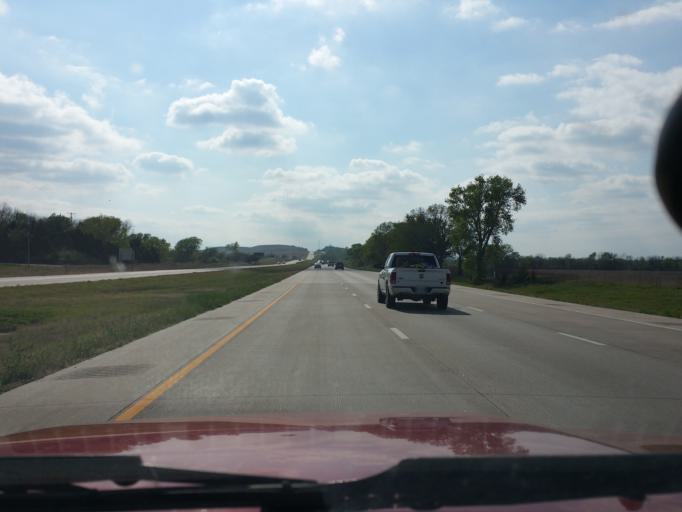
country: US
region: Kansas
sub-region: Pottawatomie County
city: Saint Marys
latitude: 39.0588
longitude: -96.0989
